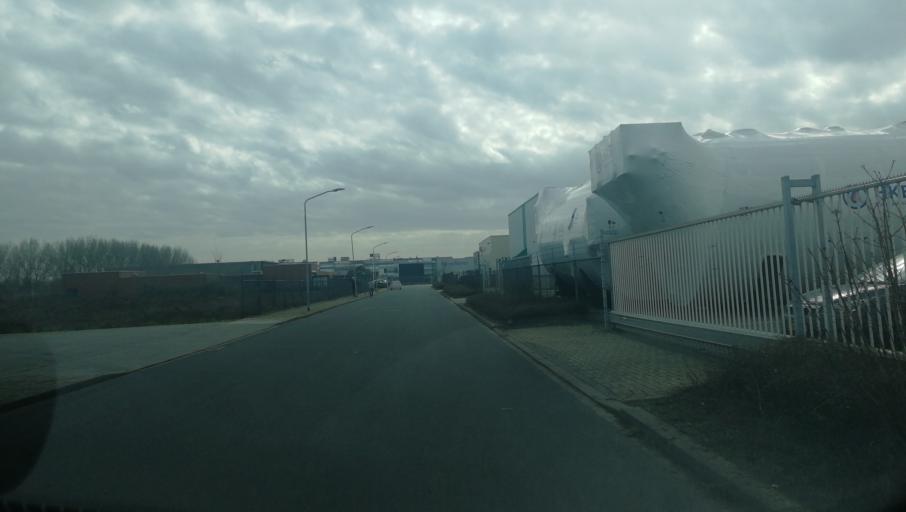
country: NL
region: Limburg
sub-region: Gemeente Venlo
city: Venlo
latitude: 51.3876
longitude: 6.1554
